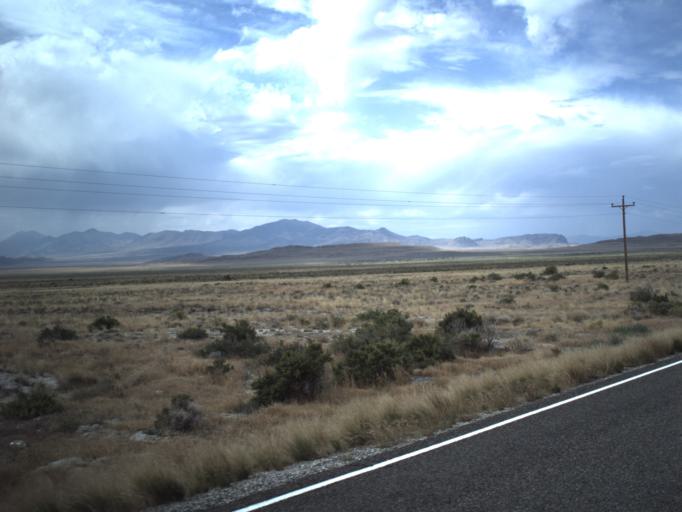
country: US
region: Utah
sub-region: Tooele County
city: Wendover
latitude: 41.4289
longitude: -113.8190
